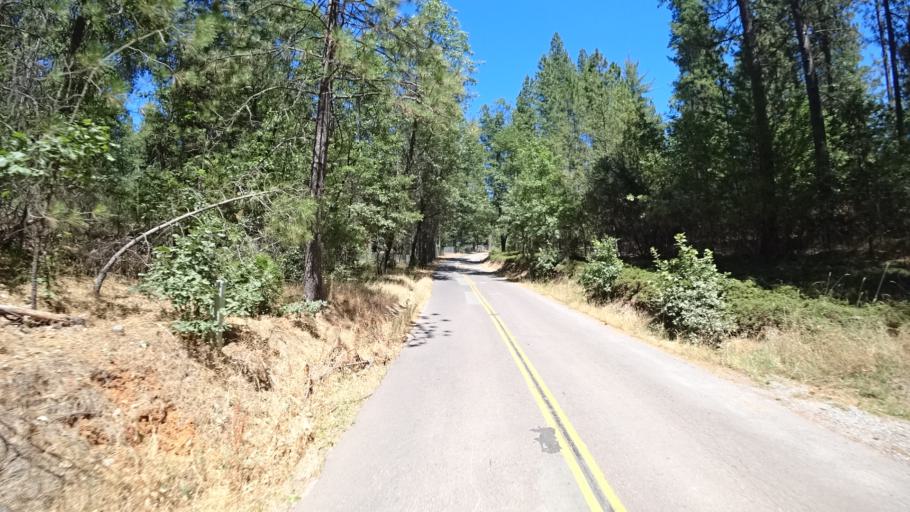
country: US
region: California
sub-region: Calaveras County
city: Mountain Ranch
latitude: 38.3200
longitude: -120.5235
